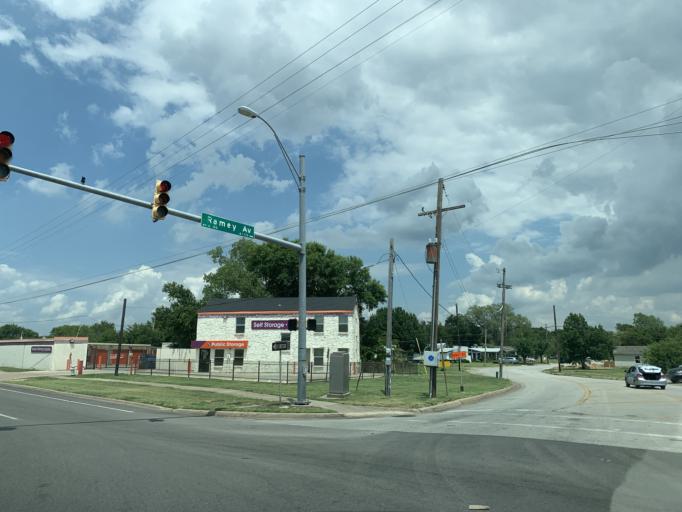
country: US
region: Texas
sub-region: Tarrant County
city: Forest Hill
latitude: 32.7204
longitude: -97.2248
